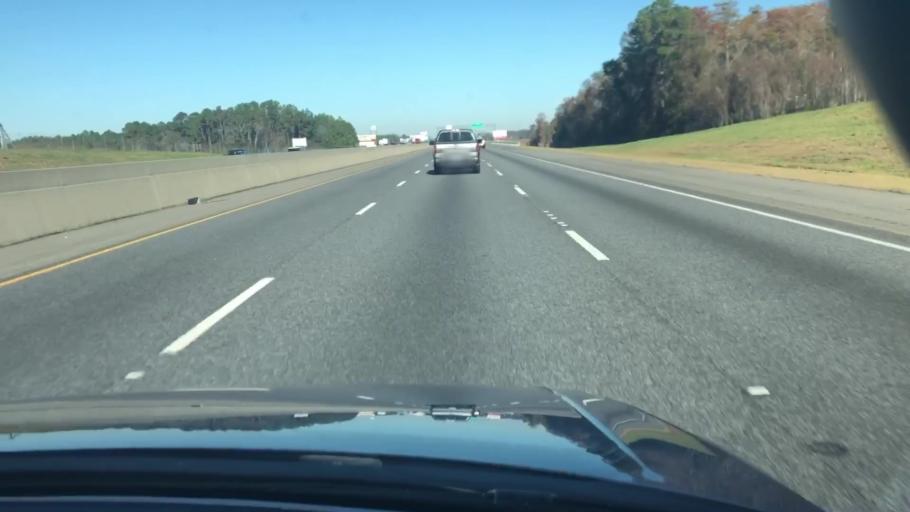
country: US
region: Georgia
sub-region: Turner County
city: Ashburn
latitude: 31.6755
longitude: -83.6151
